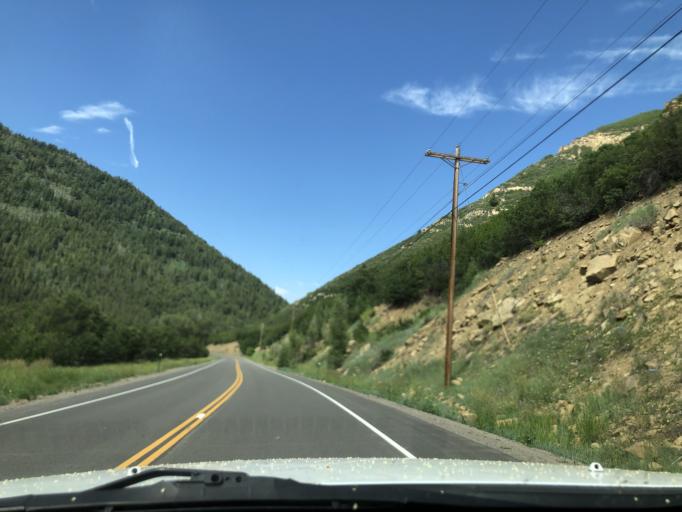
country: US
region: Colorado
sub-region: Delta County
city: Paonia
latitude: 38.9408
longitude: -107.3671
